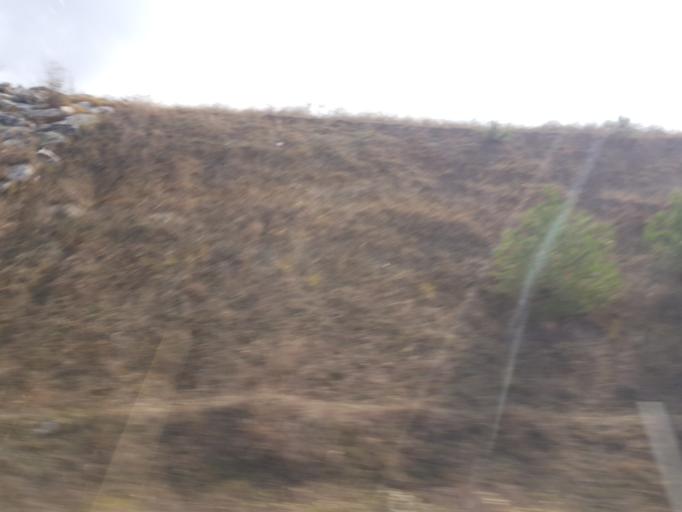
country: TR
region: Sinop
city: Sarayduzu
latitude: 41.3380
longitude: 34.8689
